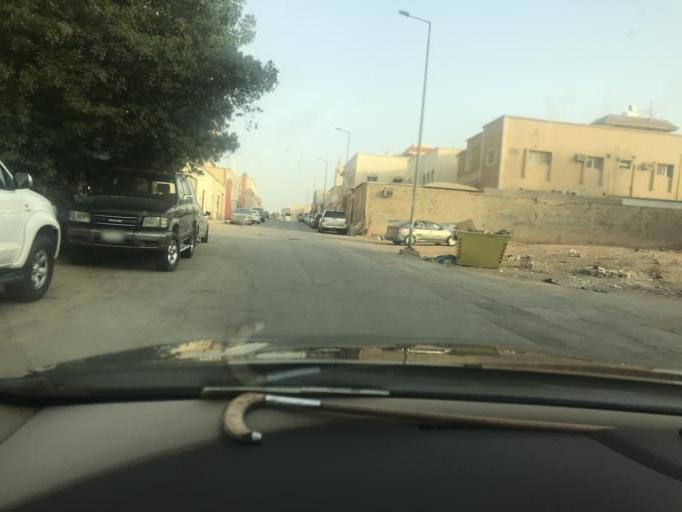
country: SA
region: Ar Riyad
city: Riyadh
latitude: 24.7362
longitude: 46.7766
